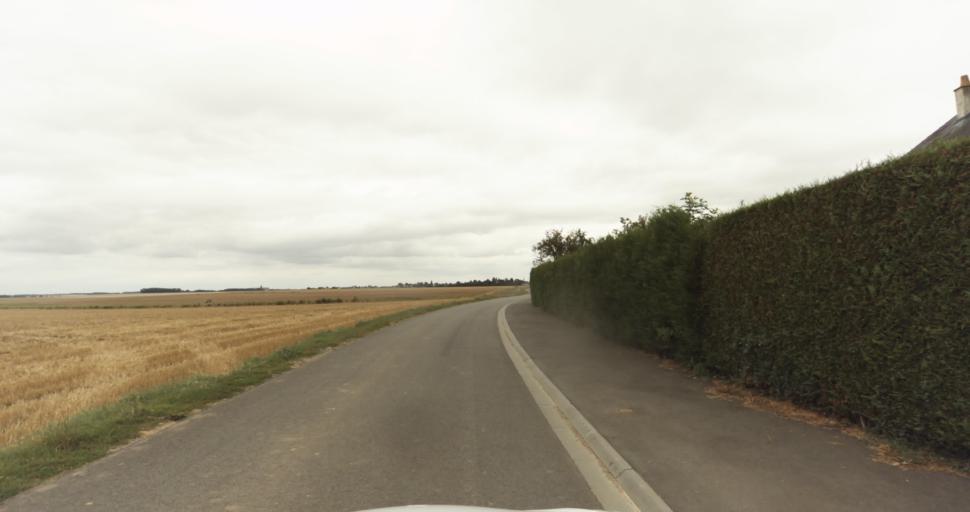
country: FR
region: Haute-Normandie
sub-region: Departement de l'Eure
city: Arnieres-sur-Iton
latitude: 48.9422
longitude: 1.1379
